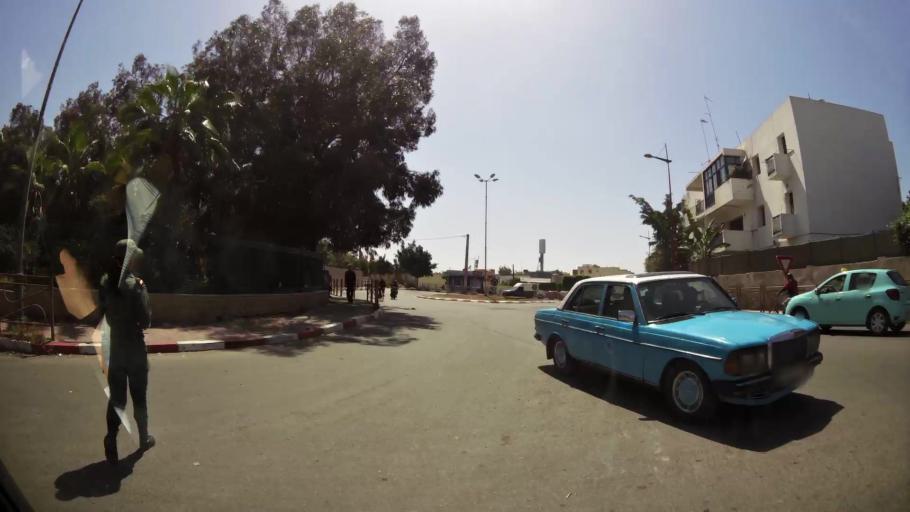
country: MA
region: Souss-Massa-Draa
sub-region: Inezgane-Ait Mellou
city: Inezgane
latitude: 30.3523
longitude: -9.5363
